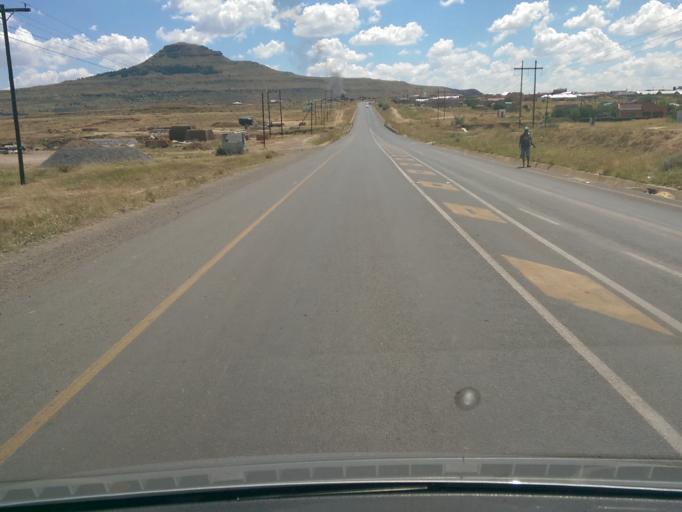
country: LS
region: Maseru
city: Maseru
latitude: -29.3765
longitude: 27.4854
